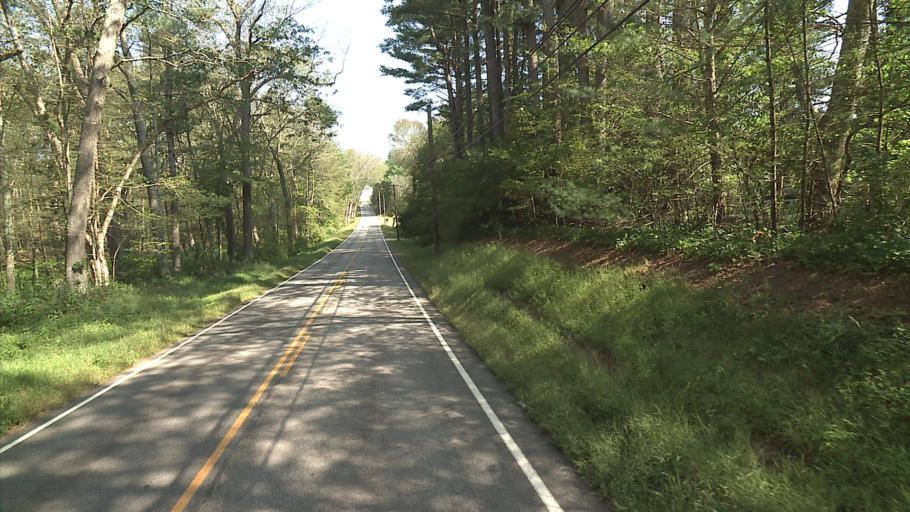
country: US
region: Connecticut
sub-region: Windham County
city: Wauregan
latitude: 41.7735
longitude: -71.9539
